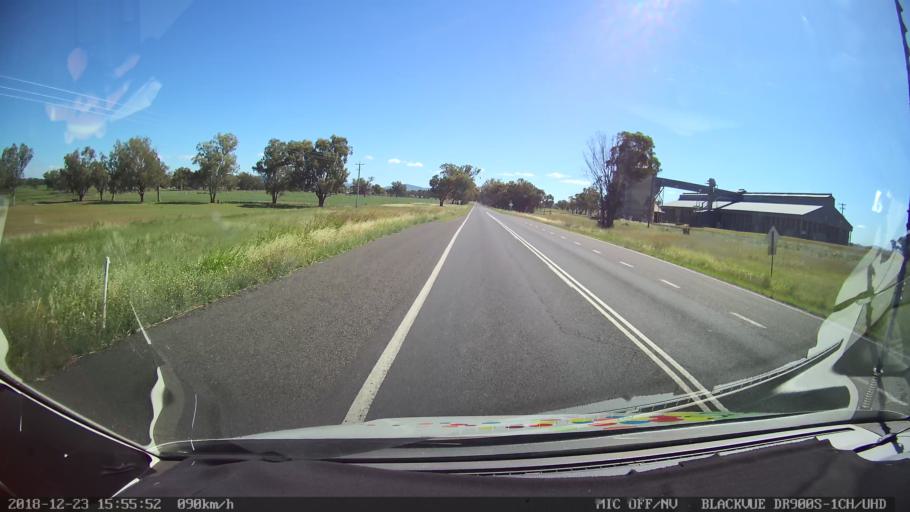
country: AU
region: New South Wales
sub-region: Tamworth Municipality
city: Phillip
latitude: -31.1599
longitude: 150.8640
